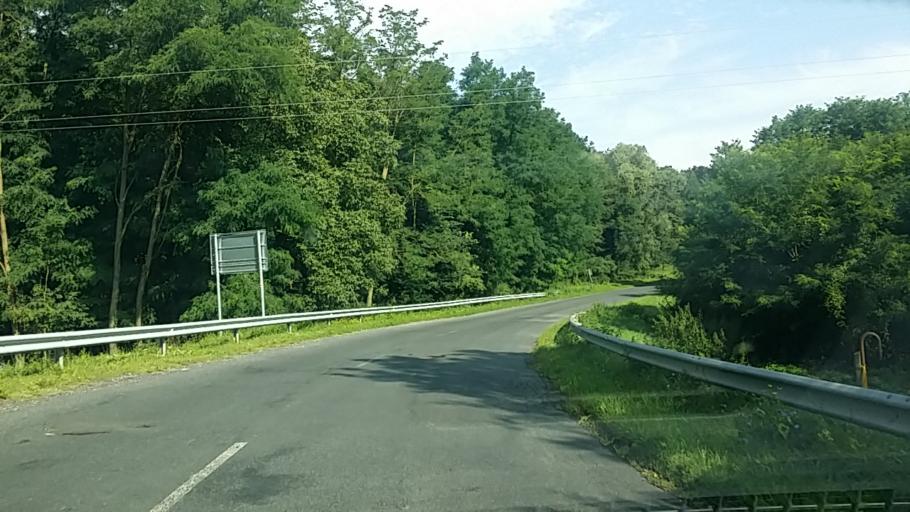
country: HU
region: Zala
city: Letenye
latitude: 46.5224
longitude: 16.7109
